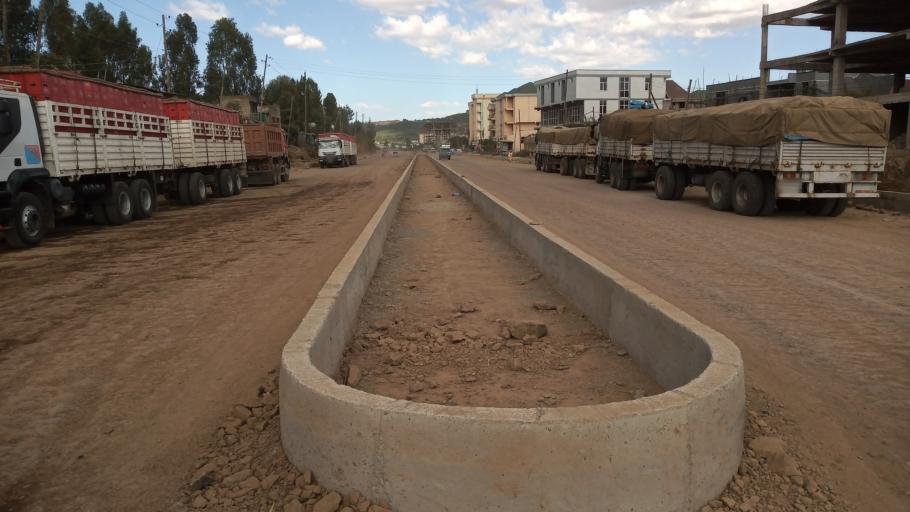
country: ET
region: Amhara
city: Gondar
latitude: 12.5640
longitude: 37.4323
